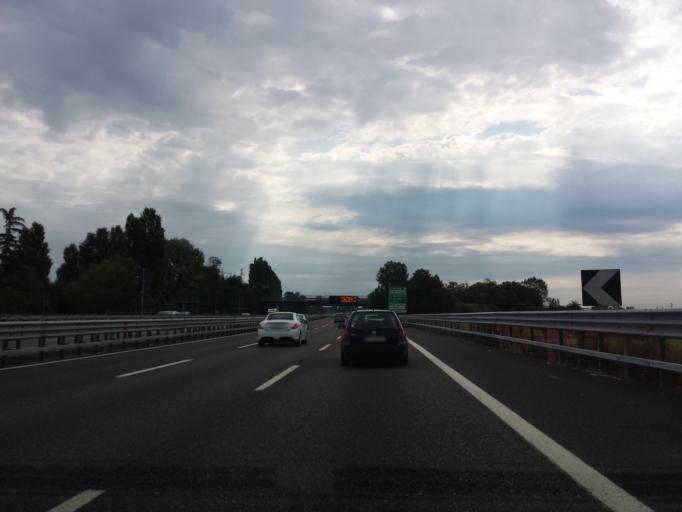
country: IT
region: Lombardy
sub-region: Citta metropolitana di Milano
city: Assago
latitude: 45.3987
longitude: 9.1292
